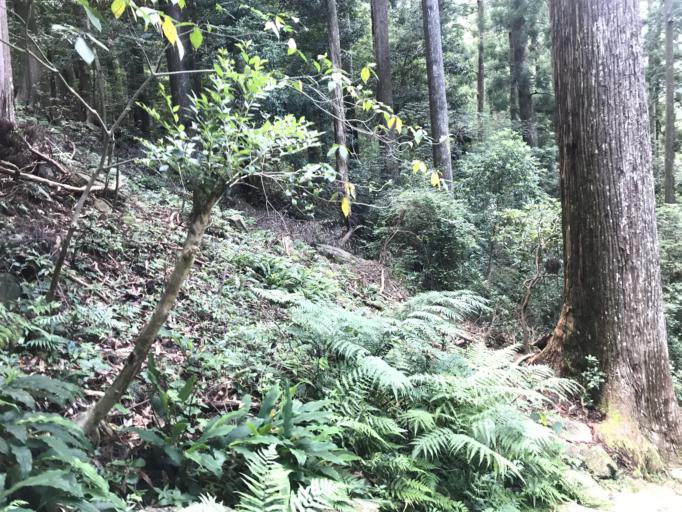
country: JP
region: Wakayama
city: Shingu
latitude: 33.6720
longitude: 135.8896
